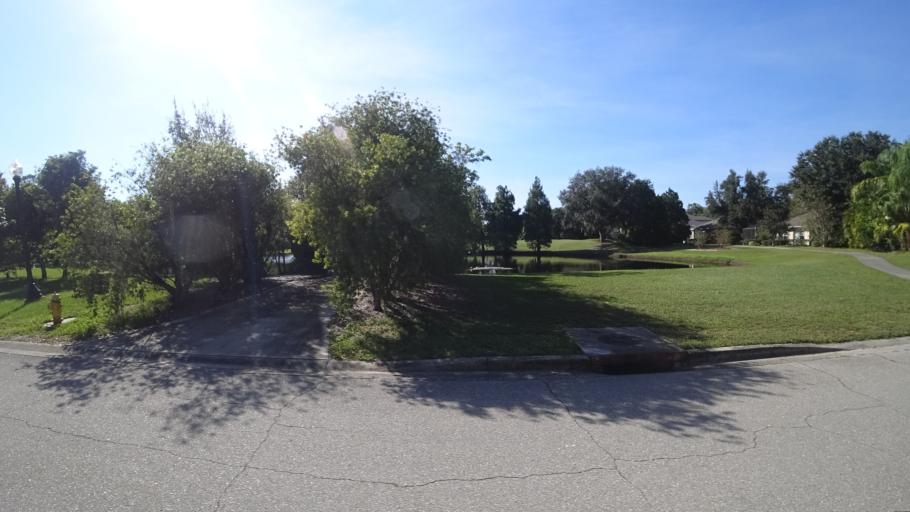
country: US
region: Florida
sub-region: Sarasota County
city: The Meadows
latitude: 27.4212
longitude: -82.4392
